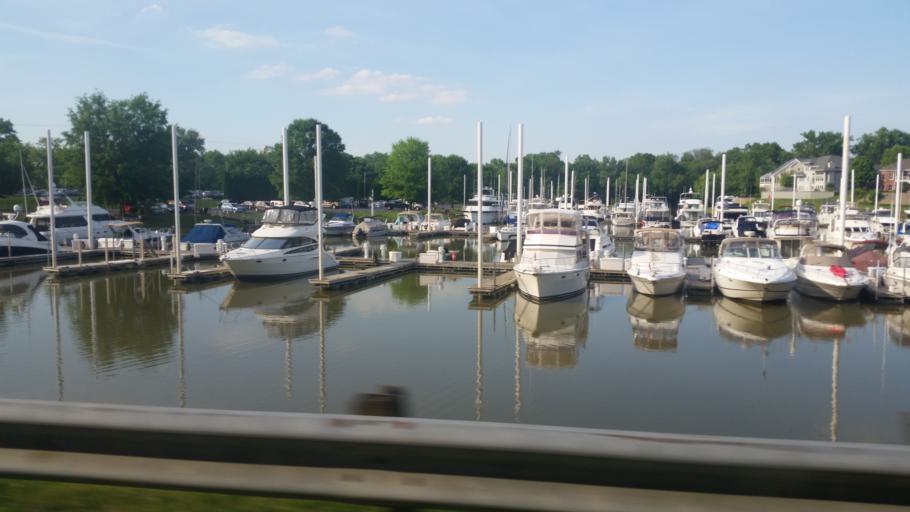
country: US
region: Kentucky
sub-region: Jefferson County
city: Prospect
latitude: 38.3288
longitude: -85.6417
